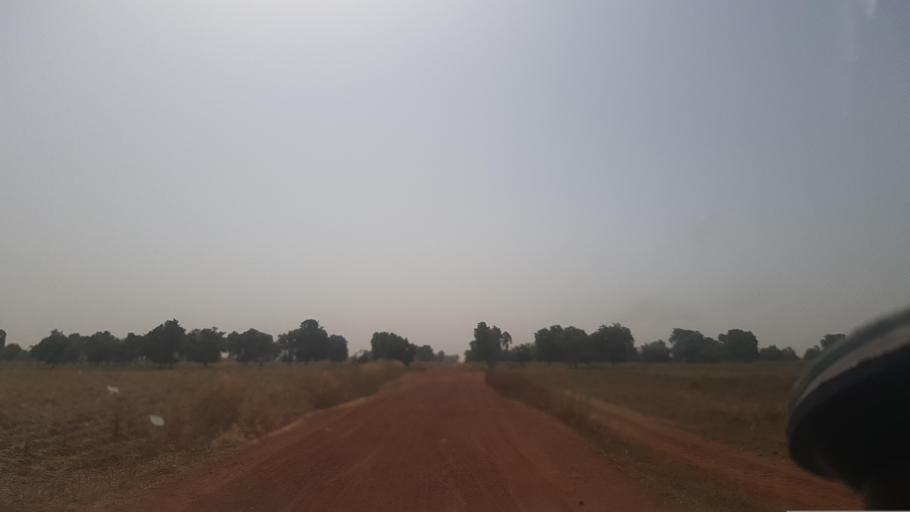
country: ML
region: Segou
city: Baroueli
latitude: 13.0061
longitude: -6.4204
